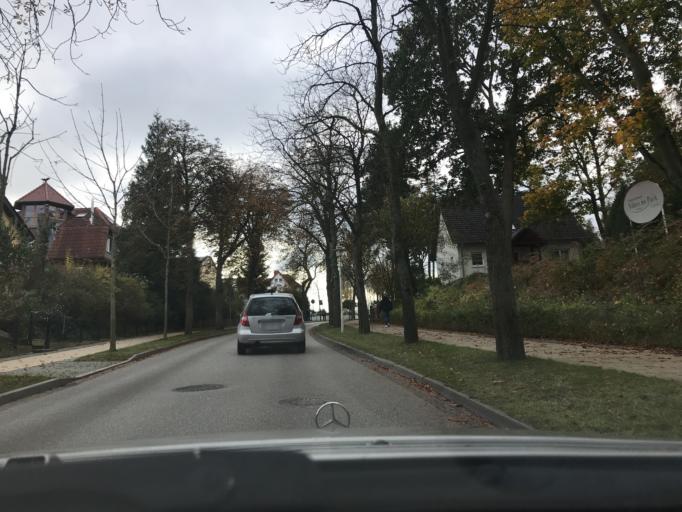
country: DE
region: Mecklenburg-Vorpommern
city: Seebad Bansin
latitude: 53.9674
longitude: 14.1364
